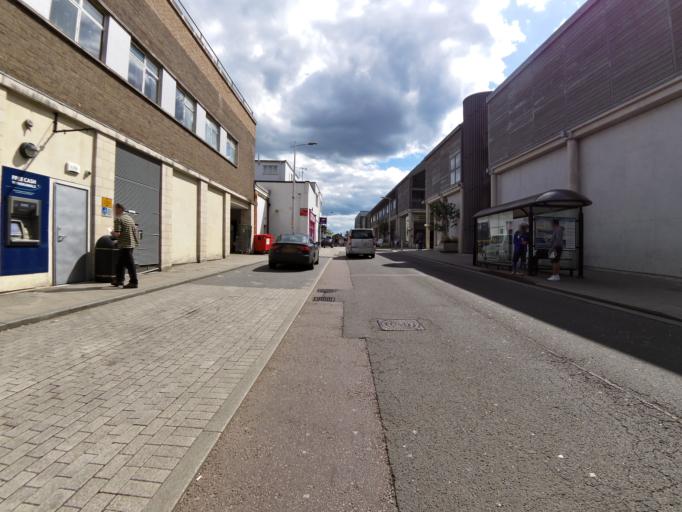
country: GB
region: England
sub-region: Suffolk
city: Bury St Edmunds
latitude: 52.2465
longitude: 0.7112
